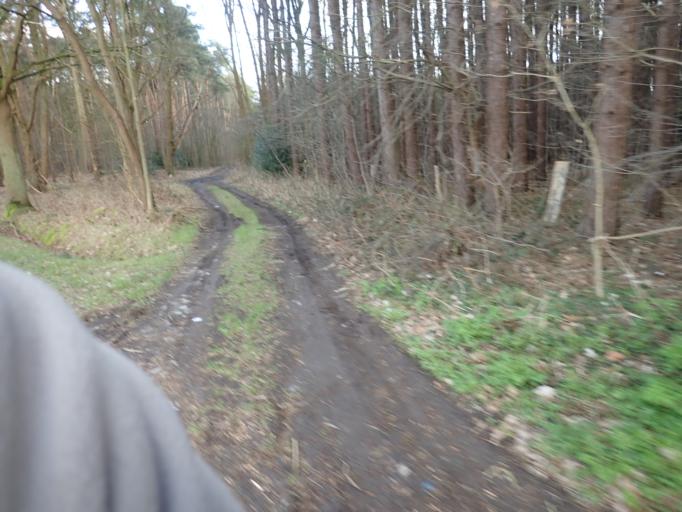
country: BE
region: Flanders
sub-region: Provincie Antwerpen
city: Zandhoven
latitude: 51.1919
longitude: 4.6758
